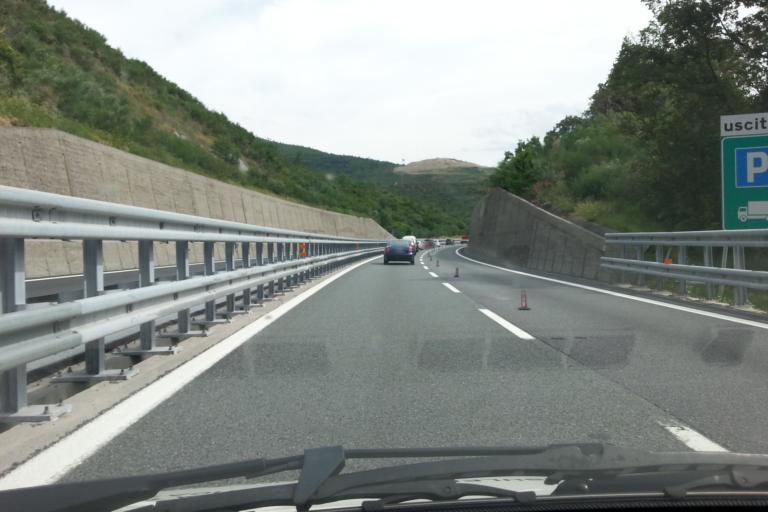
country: IT
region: Liguria
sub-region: Provincia di Savona
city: Valle di Vado
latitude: 44.2593
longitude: 8.4070
